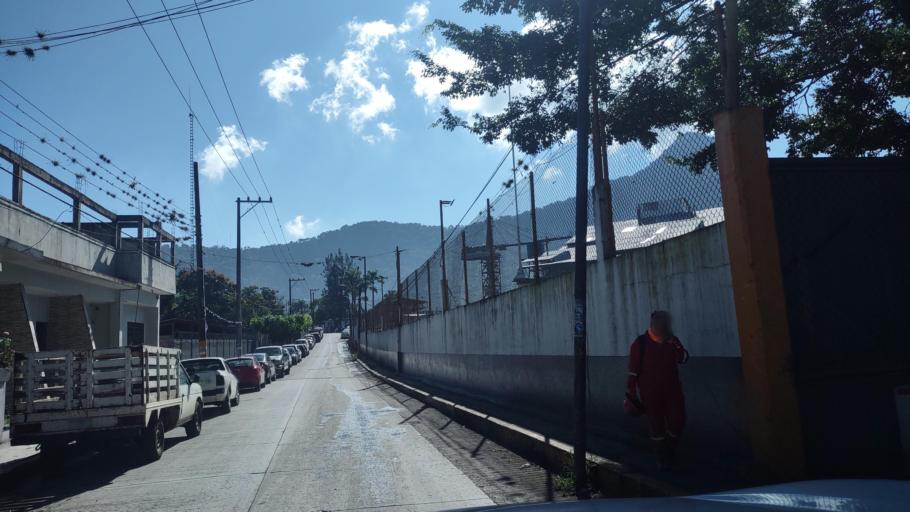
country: MX
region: Veracruz
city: Cuautlapan
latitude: 18.8740
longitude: -97.0248
